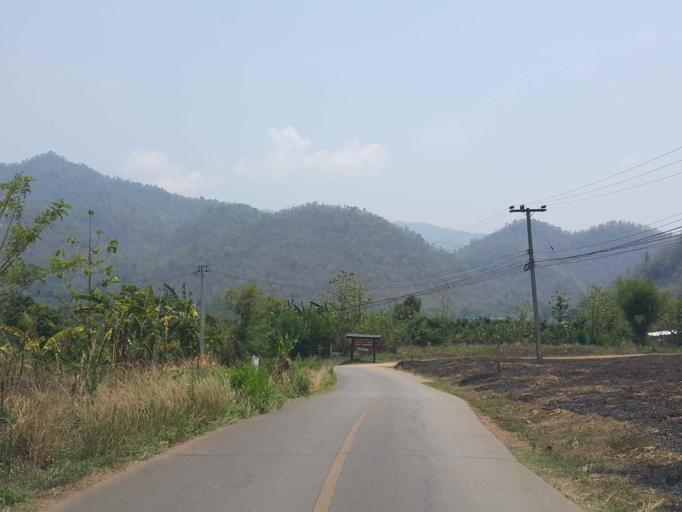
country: TH
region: Chiang Mai
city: Mae Taeng
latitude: 19.2063
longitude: 98.8537
